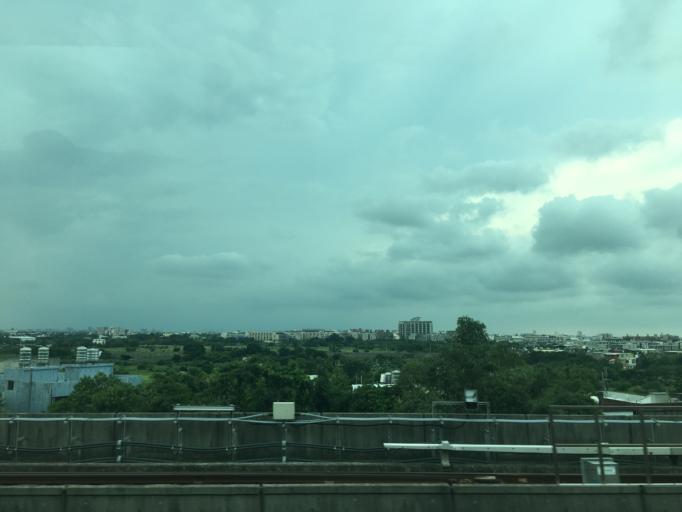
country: TW
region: Taiwan
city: Taoyuan City
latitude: 25.0861
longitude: 121.2671
